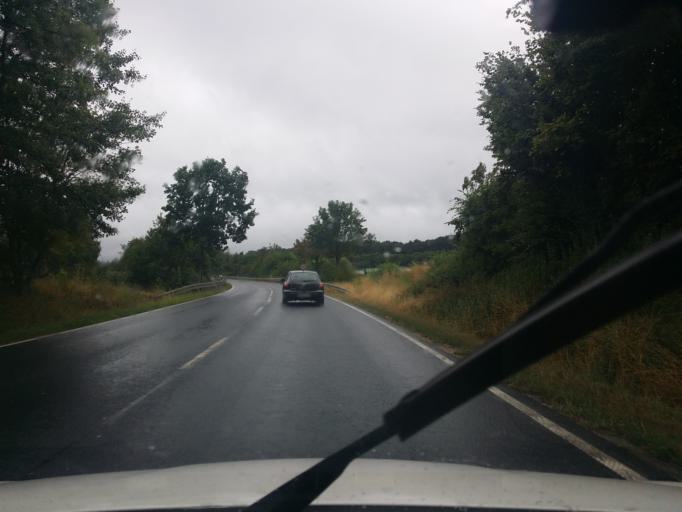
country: DE
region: Hesse
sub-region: Regierungsbezirk Darmstadt
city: Idstein
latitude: 50.2270
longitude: 8.2555
